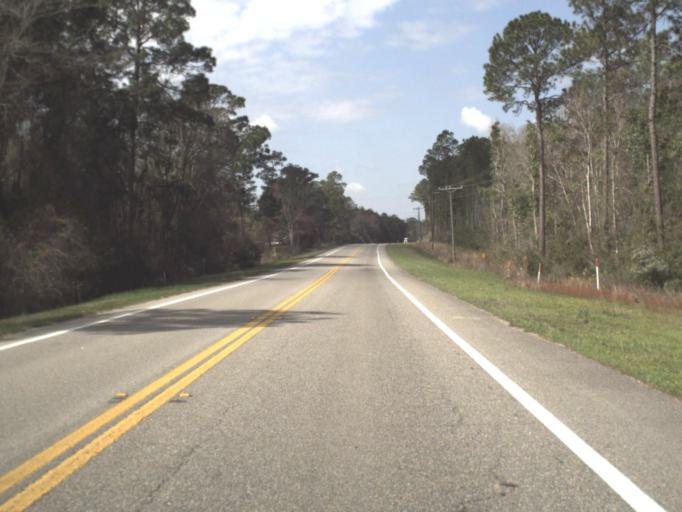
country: US
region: Florida
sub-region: Gadsden County
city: Gretna
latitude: 30.3842
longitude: -84.7239
